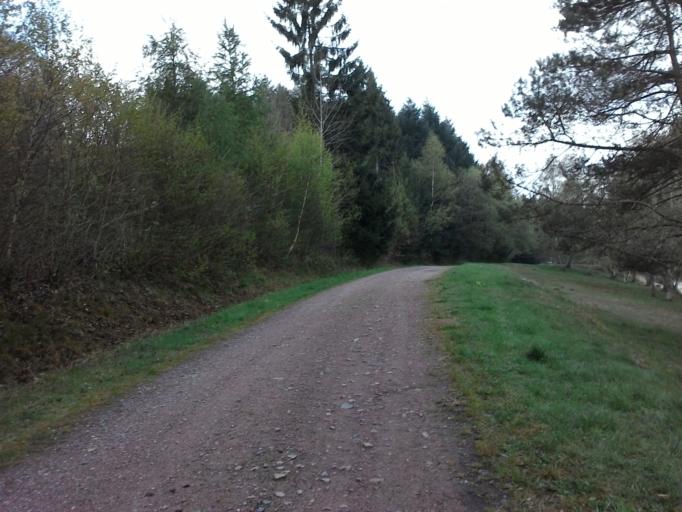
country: FR
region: Bourgogne
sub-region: Departement de la Cote-d'Or
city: Saulieu
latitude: 47.2438
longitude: 4.1914
